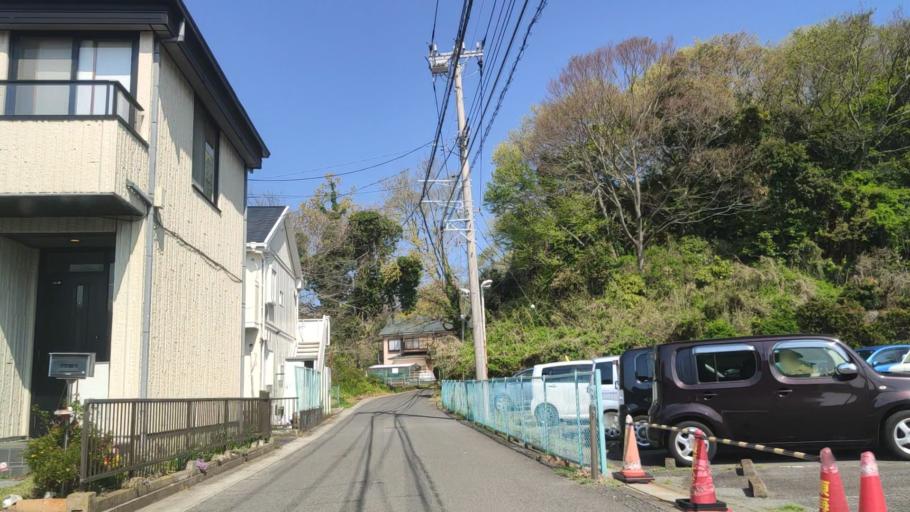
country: JP
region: Kanagawa
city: Ninomiya
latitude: 35.3109
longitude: 139.2730
